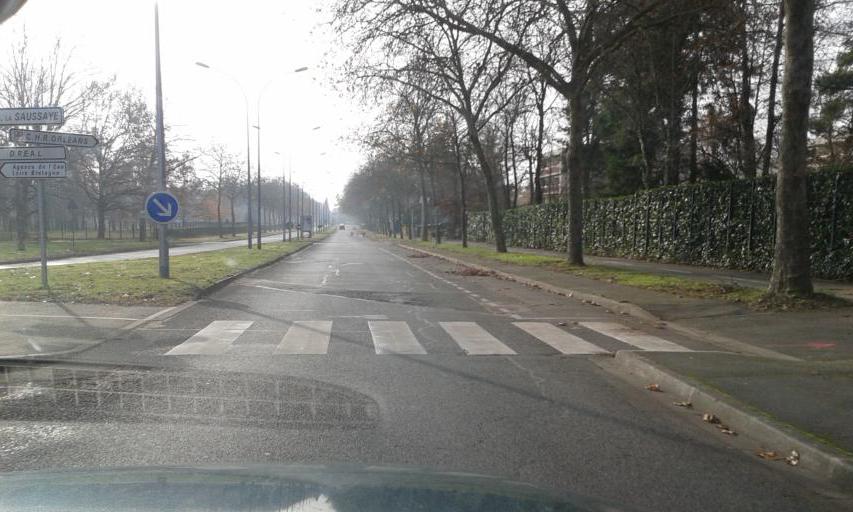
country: FR
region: Centre
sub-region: Departement du Loiret
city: Saint-Cyr-en-Val
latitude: 47.8289
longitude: 1.9363
